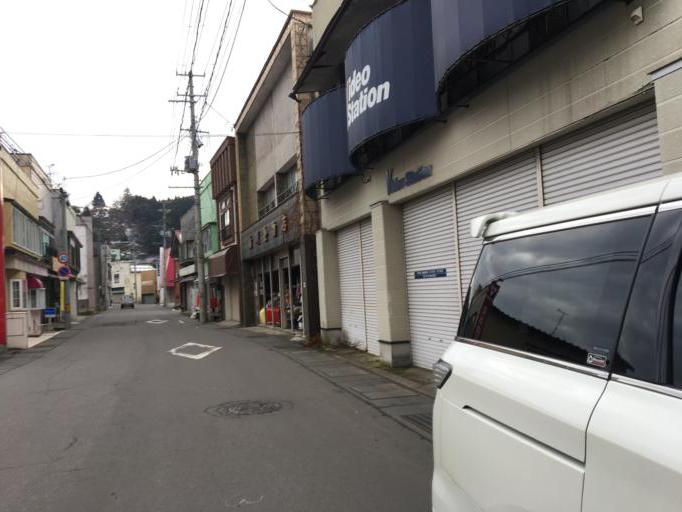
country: JP
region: Aomori
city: Hirosaki
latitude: 40.5205
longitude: 140.5673
